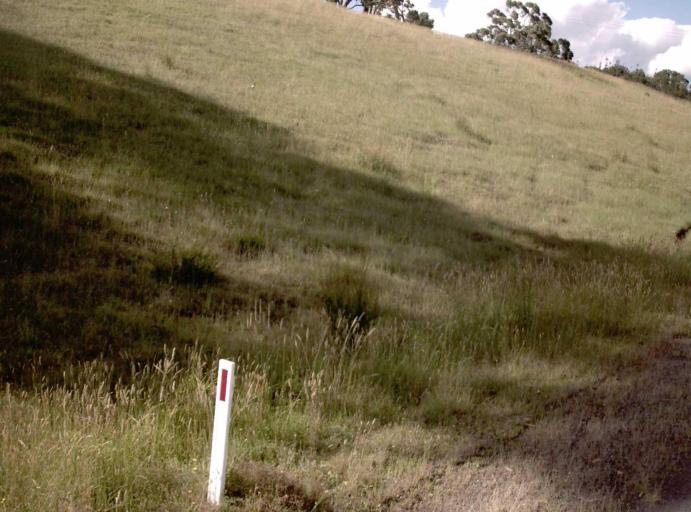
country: AU
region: Victoria
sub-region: Latrobe
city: Moe
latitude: -38.1943
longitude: 146.3266
